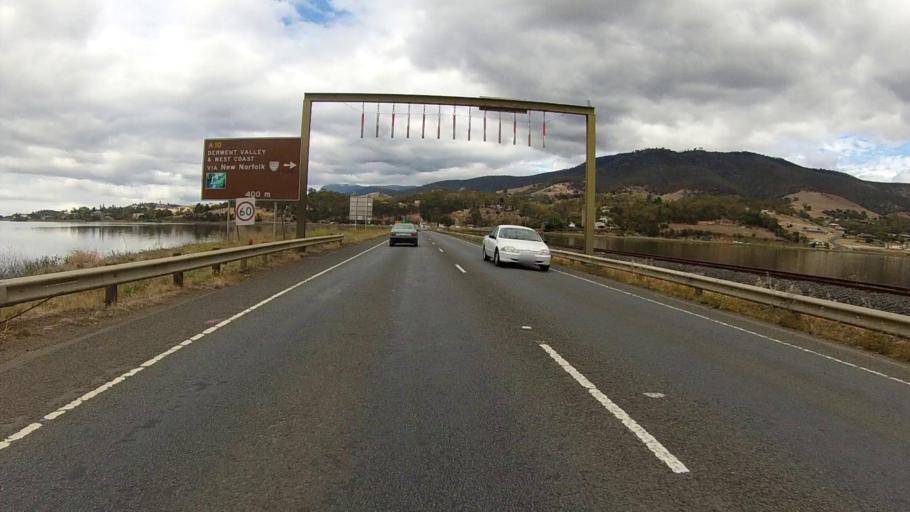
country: AU
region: Tasmania
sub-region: Brighton
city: Bridgewater
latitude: -42.7443
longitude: 147.2251
